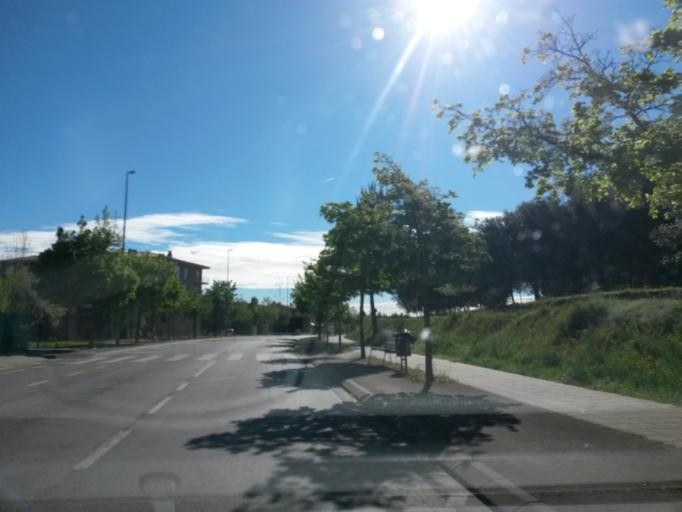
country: ES
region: Catalonia
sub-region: Provincia de Girona
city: Celra
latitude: 42.0266
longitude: 2.8889
